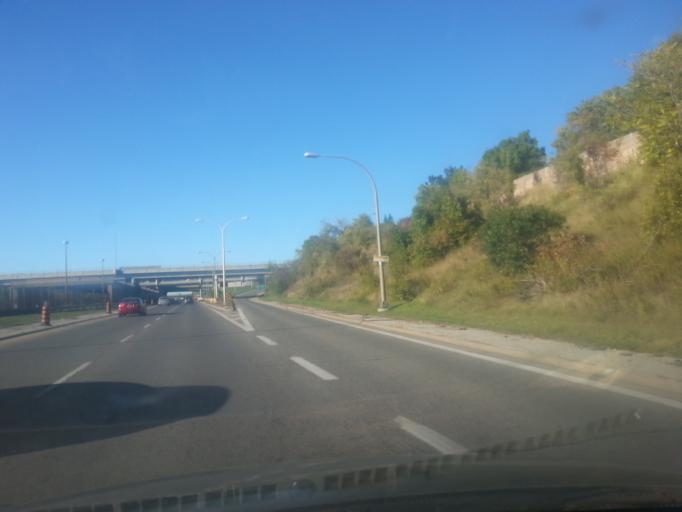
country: CA
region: Ontario
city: Toronto
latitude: 43.7131
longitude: -79.4429
